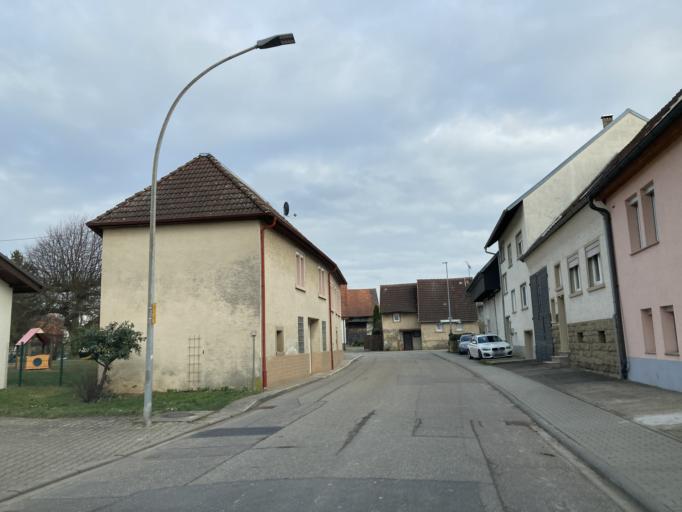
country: DE
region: Baden-Wuerttemberg
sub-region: Karlsruhe Region
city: Sulzfeld
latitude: 49.1395
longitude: 8.8555
